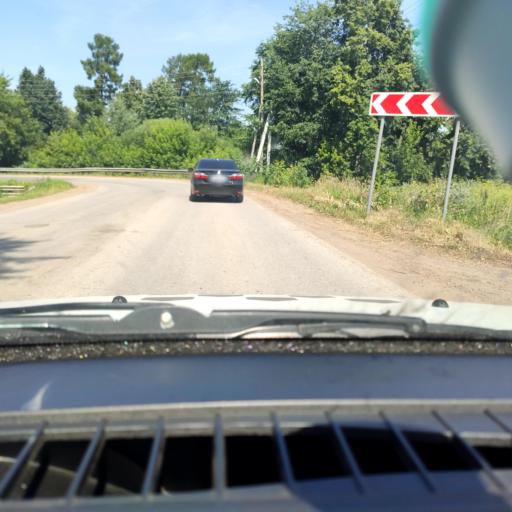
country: RU
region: Perm
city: Okhansk
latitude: 57.7263
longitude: 55.3881
